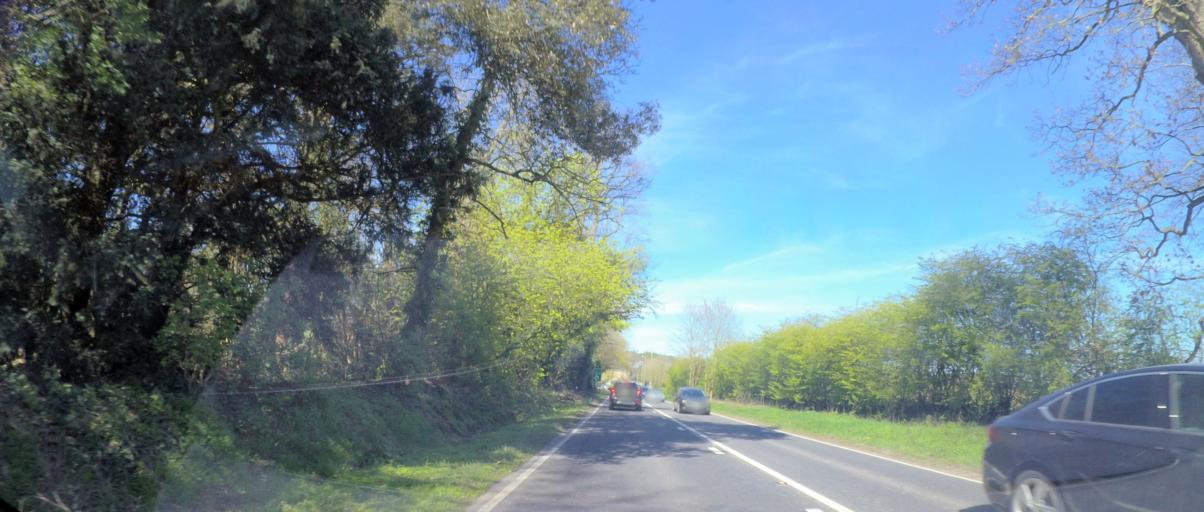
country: GB
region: England
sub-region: Hampshire
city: Old Basing
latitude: 51.2991
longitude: -1.0424
